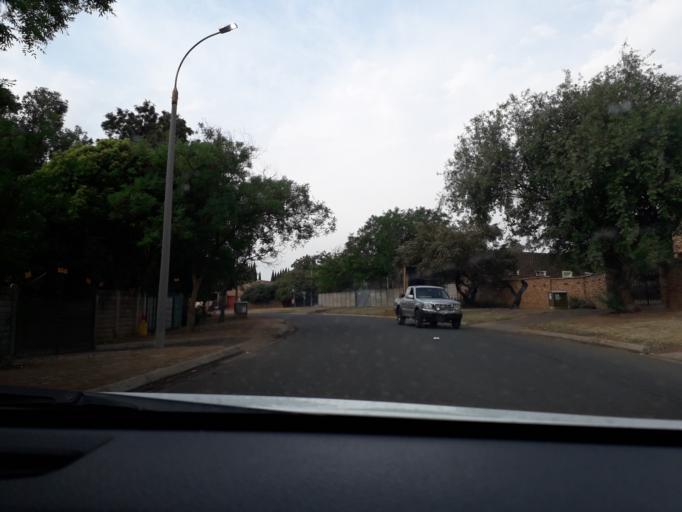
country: ZA
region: Gauteng
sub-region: City of Johannesburg Metropolitan Municipality
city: Modderfontein
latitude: -26.0567
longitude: 28.2011
